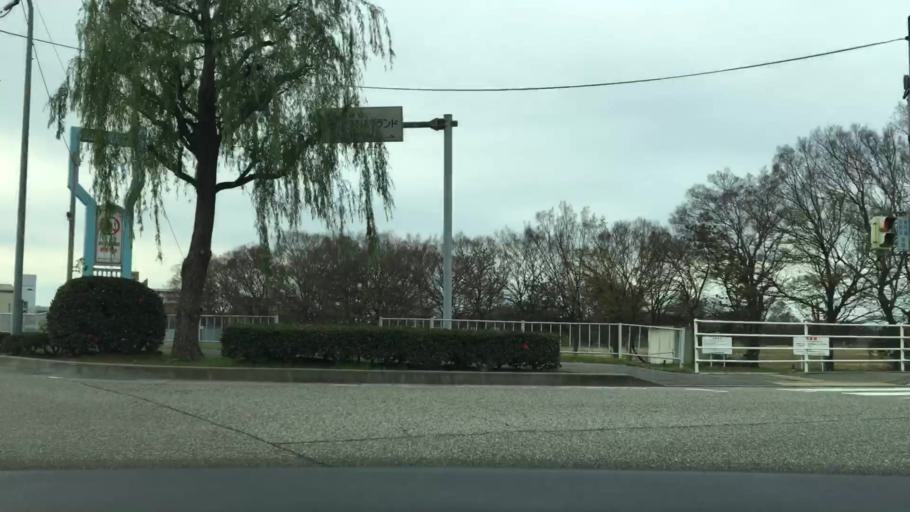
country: JP
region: Ishikawa
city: Kanazawa-shi
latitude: 36.5698
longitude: 136.6362
